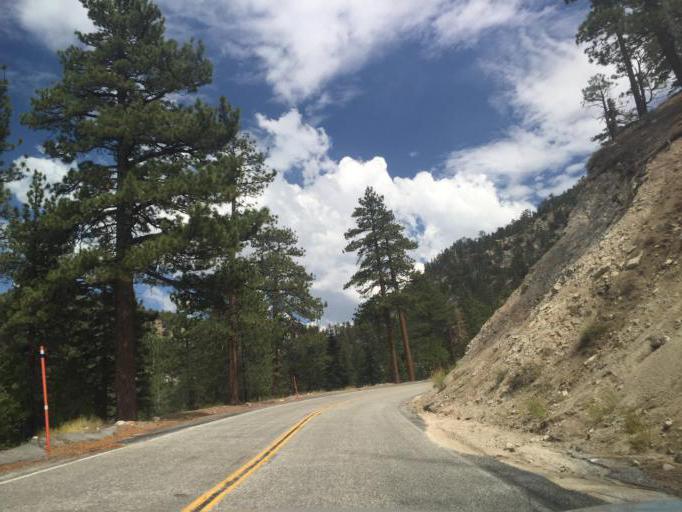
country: US
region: California
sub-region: Los Angeles County
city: Littlerock
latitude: 34.3485
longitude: -117.9464
